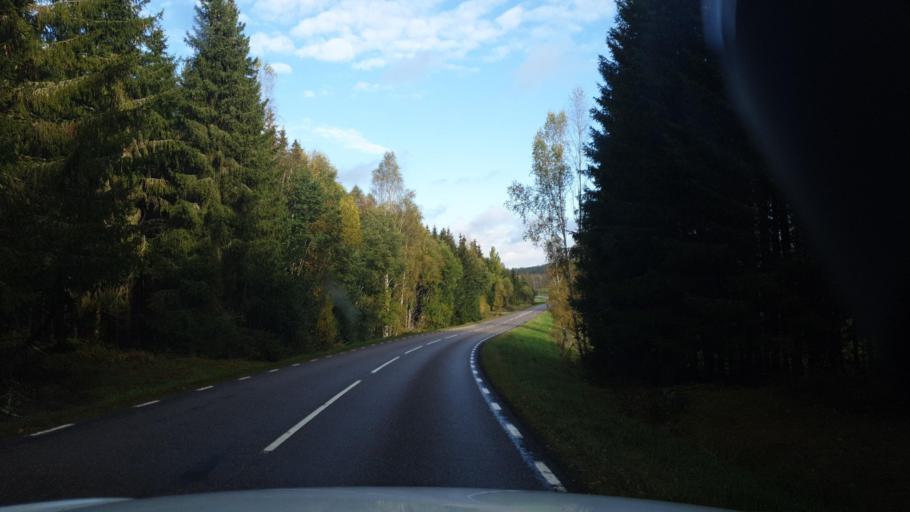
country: SE
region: Vaermland
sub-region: Arvika Kommun
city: Arvika
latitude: 59.4921
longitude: 12.6839
